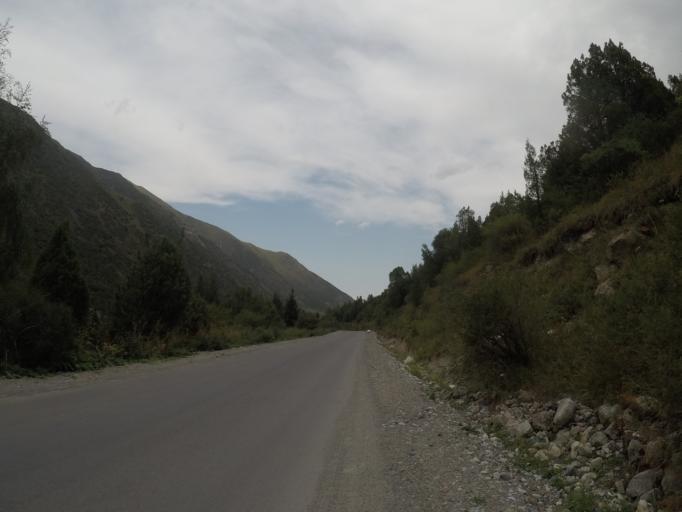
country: KG
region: Chuy
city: Bishkek
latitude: 42.5870
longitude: 74.4841
